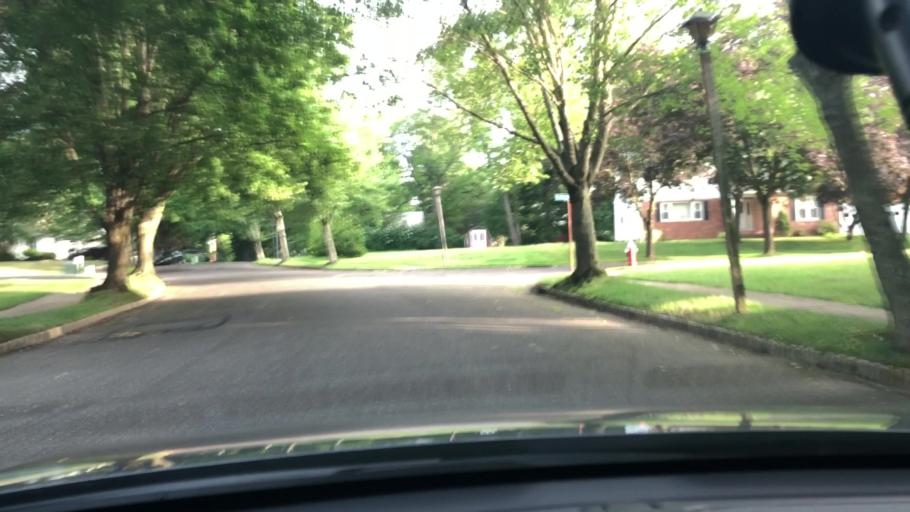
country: US
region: New Jersey
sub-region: Middlesex County
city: East Brunswick
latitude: 40.4210
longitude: -74.4274
